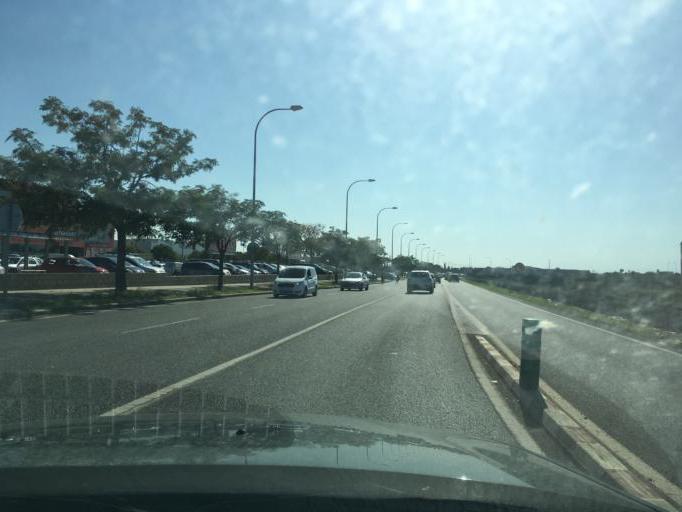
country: ES
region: Balearic Islands
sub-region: Illes Balears
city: Palma
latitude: 39.5739
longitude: 2.6853
